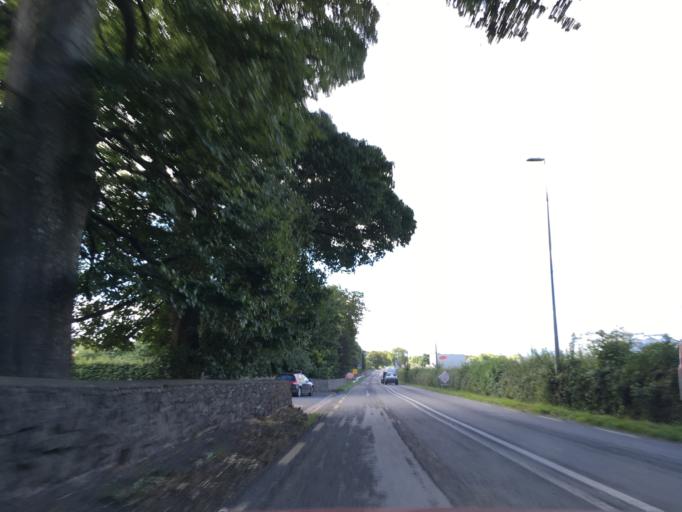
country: IE
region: Munster
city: Cahir
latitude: 52.4372
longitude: -7.8836
